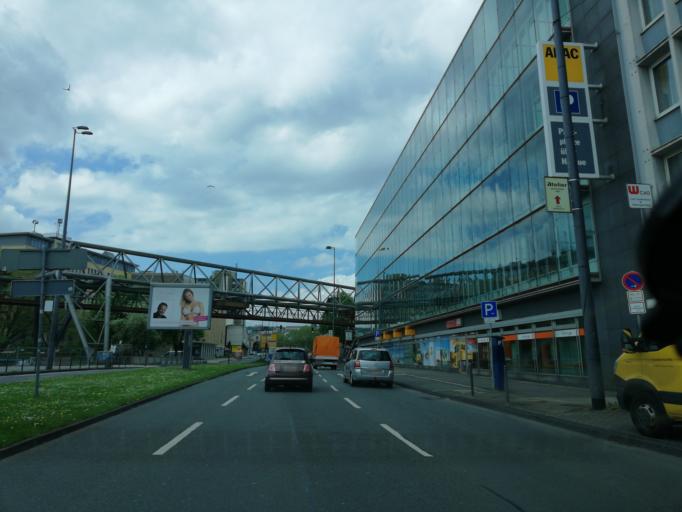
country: DE
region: North Rhine-Westphalia
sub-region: Regierungsbezirk Dusseldorf
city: Wuppertal
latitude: 51.2563
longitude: 7.1552
